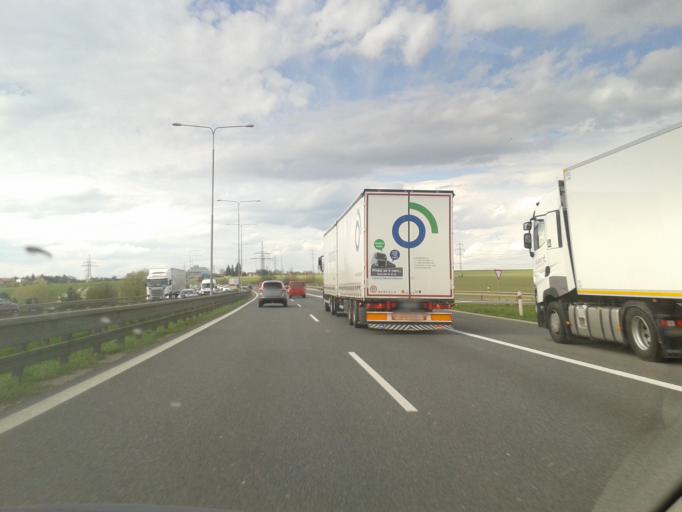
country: CZ
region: Central Bohemia
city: Rudna
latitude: 50.0308
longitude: 14.2841
